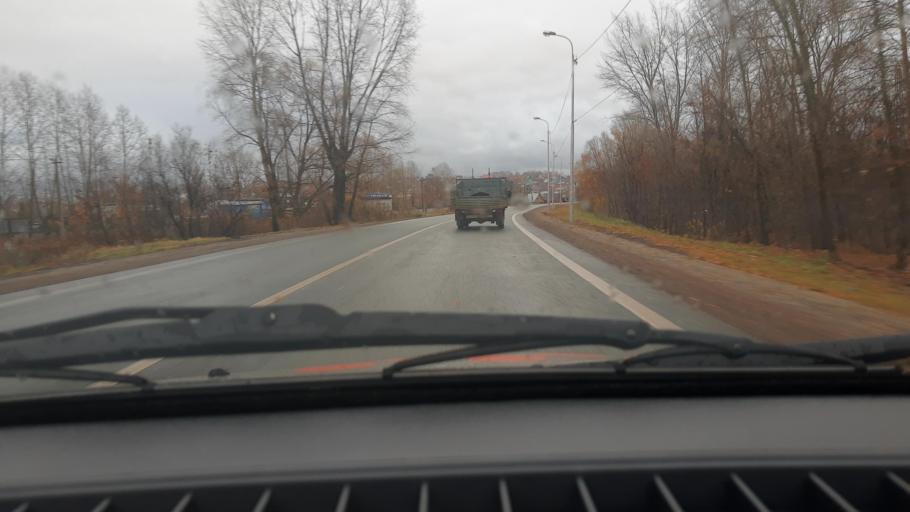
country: RU
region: Bashkortostan
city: Ufa
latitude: 54.8387
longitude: 56.1293
